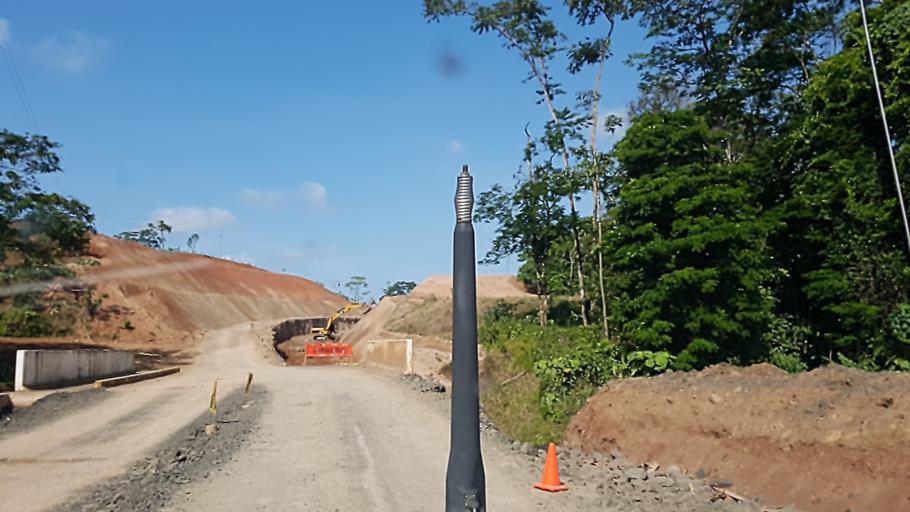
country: NI
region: Atlantico Sur
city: Nueva Guinea
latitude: 11.8041
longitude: -84.1221
